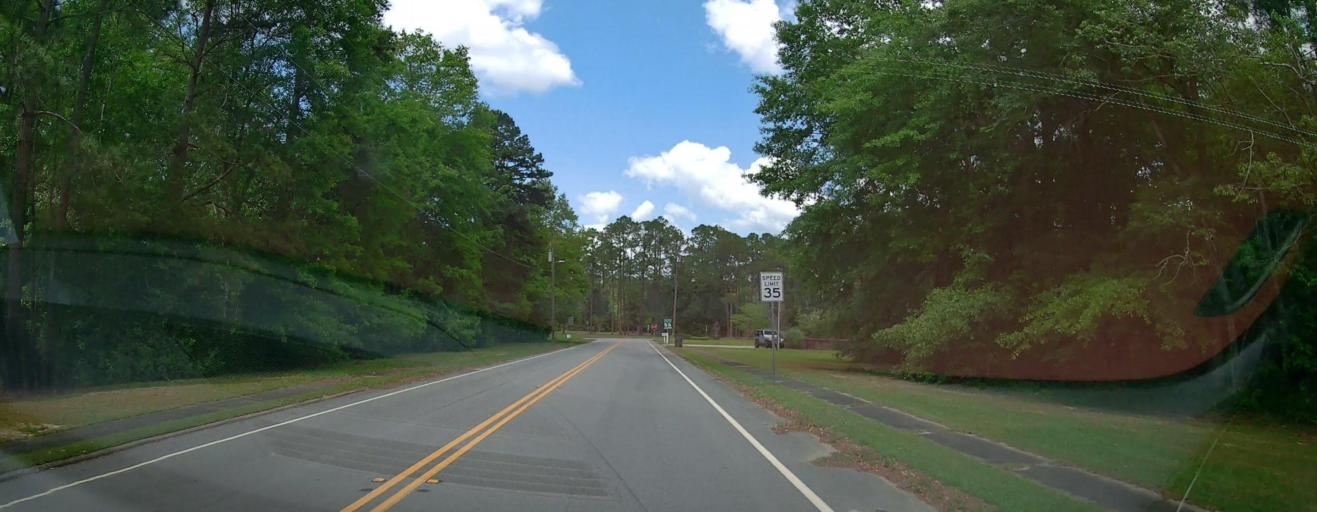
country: US
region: Georgia
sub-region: Treutlen County
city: Soperton
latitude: 32.3817
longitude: -82.5836
